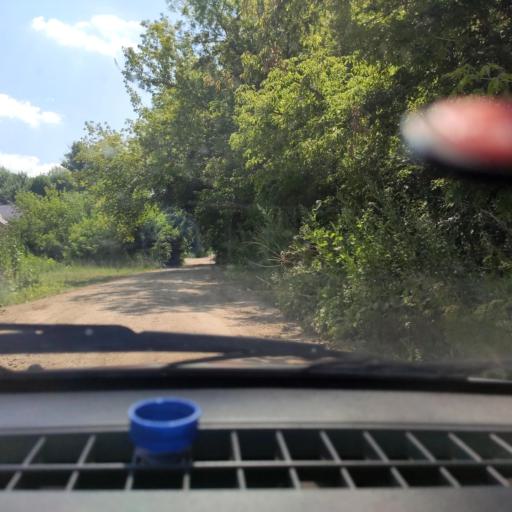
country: RU
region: Bashkortostan
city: Ufa
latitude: 54.6840
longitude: 55.9538
